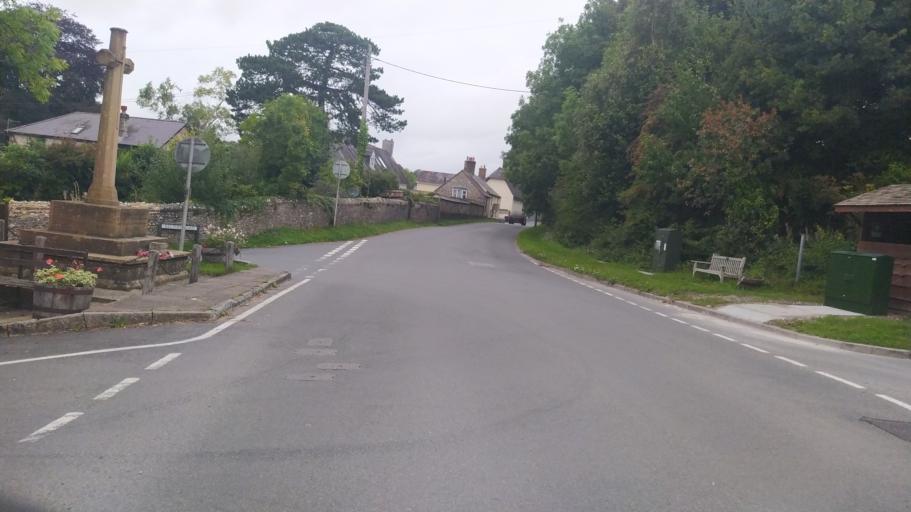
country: GB
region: England
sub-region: Dorset
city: Dorchester
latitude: 50.7739
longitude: -2.4045
